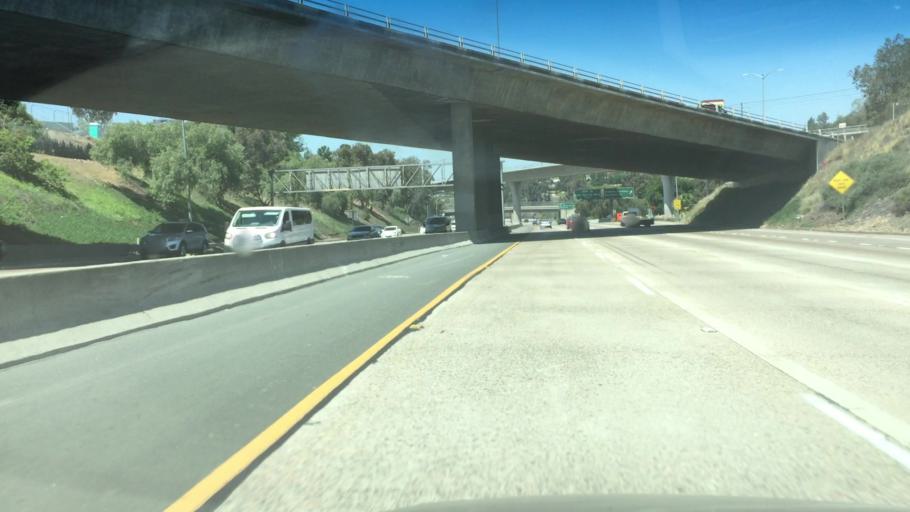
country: US
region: California
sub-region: San Diego County
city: La Mesa
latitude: 32.7717
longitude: -117.0262
